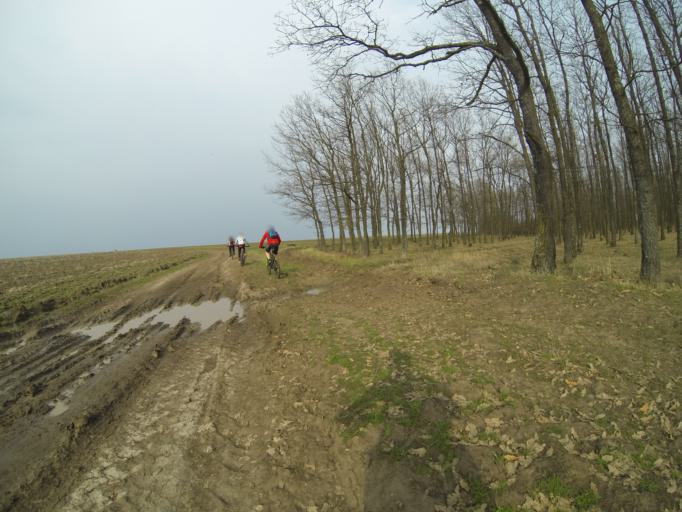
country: RO
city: Varvoru
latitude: 44.2588
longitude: 23.6874
